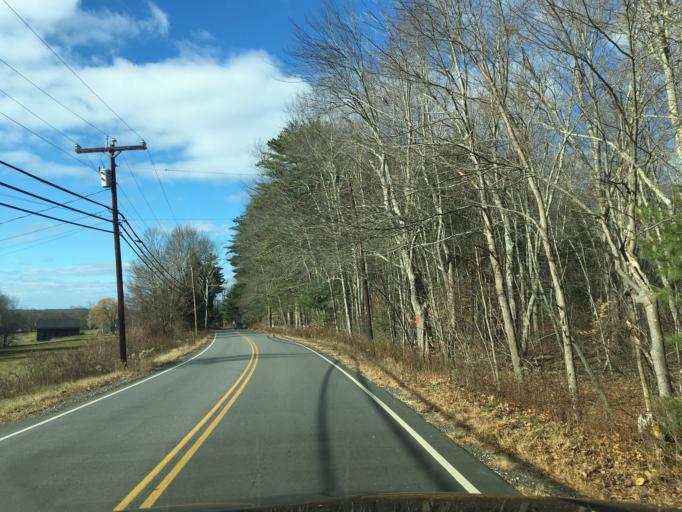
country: US
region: New Hampshire
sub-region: Rockingham County
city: Stratham Station
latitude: 43.0245
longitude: -70.9022
